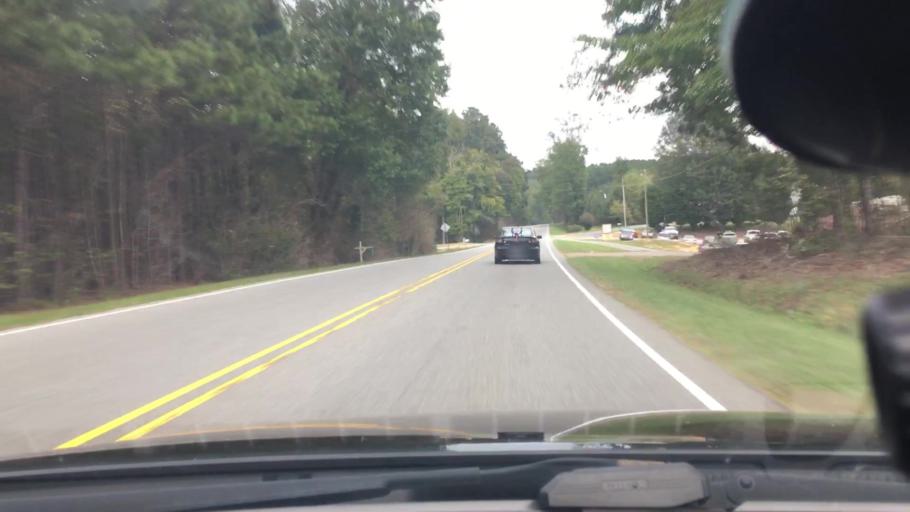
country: US
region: North Carolina
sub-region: Moore County
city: Robbins
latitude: 35.3895
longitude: -79.6472
